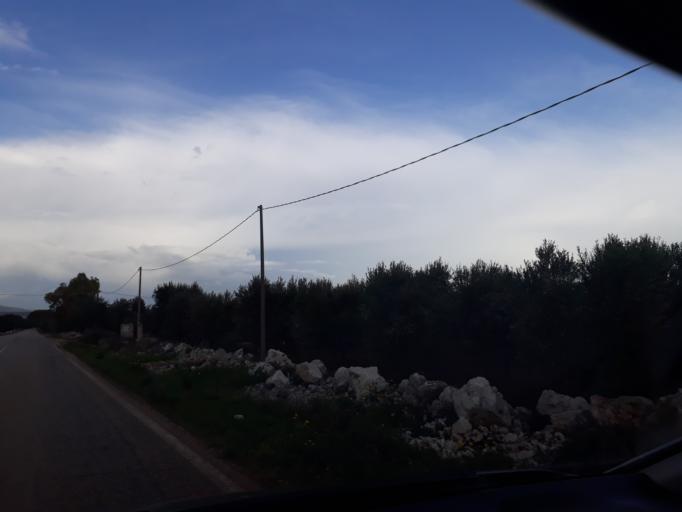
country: IT
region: Apulia
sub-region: Provincia di Brindisi
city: Pezze di Greco
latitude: 40.8039
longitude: 17.3944
